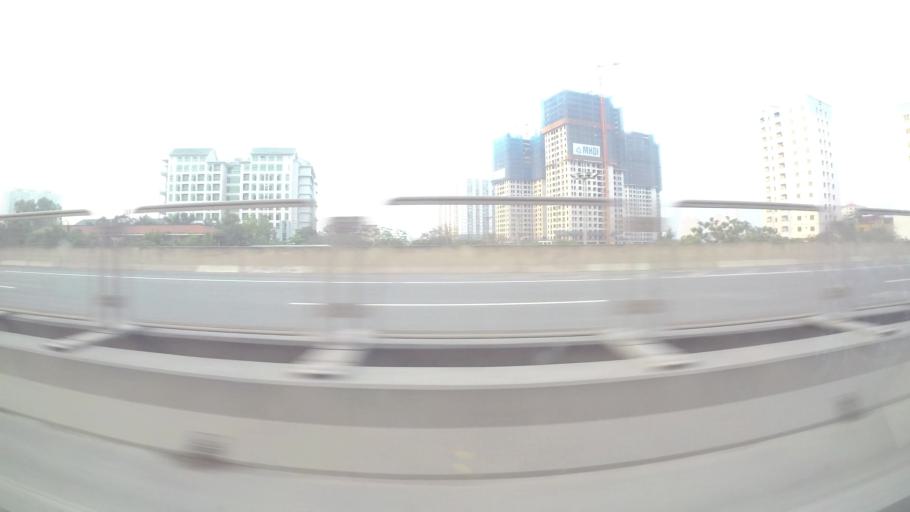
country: VN
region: Ha Noi
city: Van Dien
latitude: 20.9709
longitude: 105.8245
